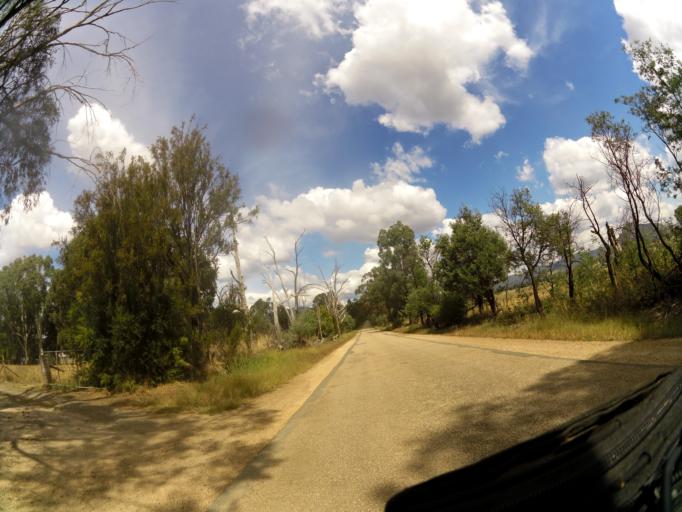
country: AU
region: Victoria
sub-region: Benalla
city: Benalla
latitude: -36.7632
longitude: 145.9766
